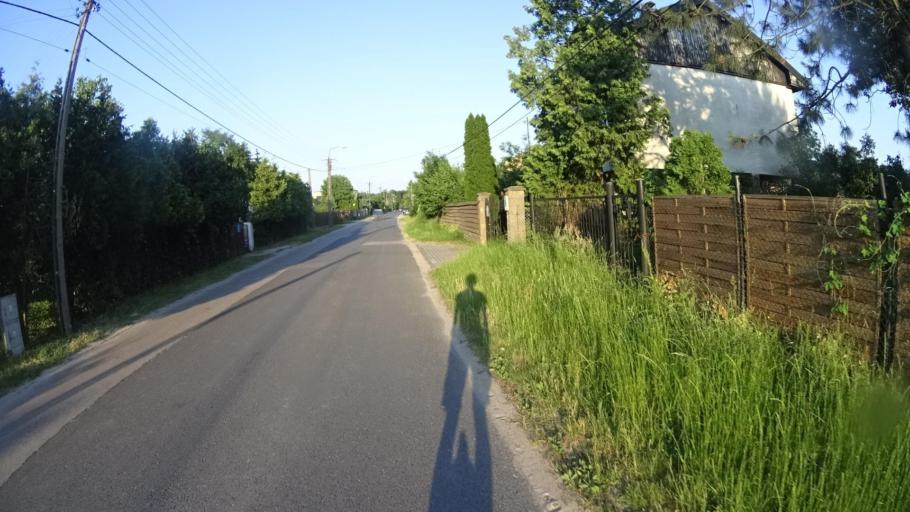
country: PL
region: Masovian Voivodeship
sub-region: Powiat warszawski zachodni
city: Stare Babice
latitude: 52.2653
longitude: 20.8480
